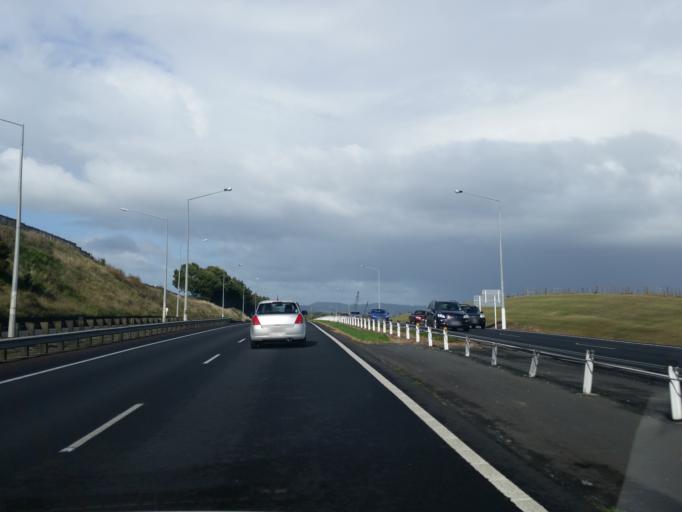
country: NZ
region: Auckland
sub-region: Auckland
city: Papakura
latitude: -37.0898
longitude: 174.9403
